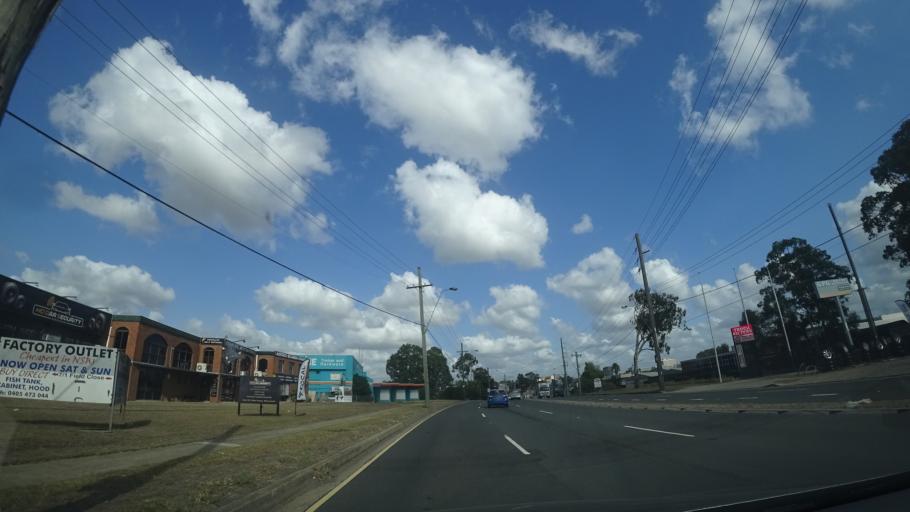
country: AU
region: New South Wales
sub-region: Fairfield
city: Liverpool
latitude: -33.9298
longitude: 150.9379
